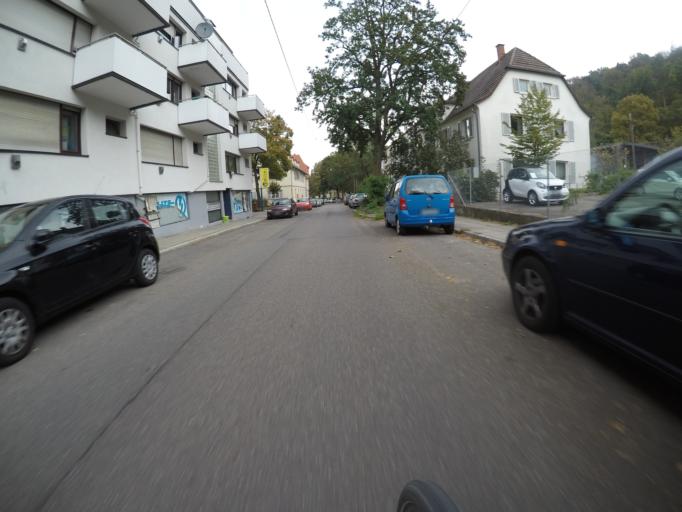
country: DE
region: Baden-Wuerttemberg
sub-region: Regierungsbezirk Stuttgart
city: Stuttgart
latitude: 48.7564
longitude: 9.1458
